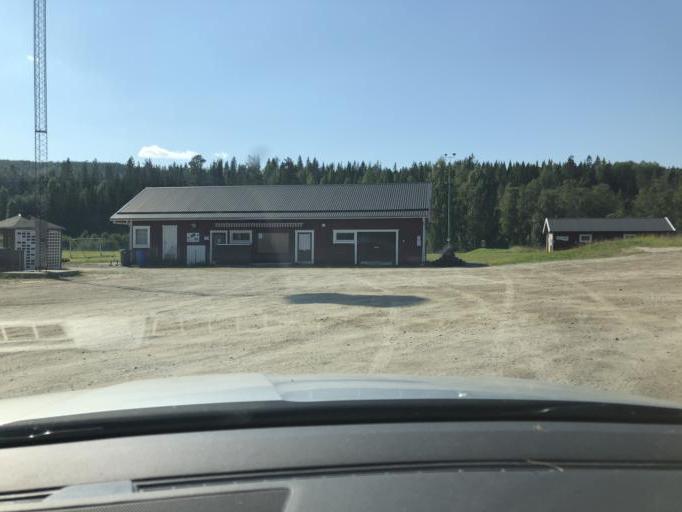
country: SE
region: Vaesternorrland
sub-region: OErnskoeldsviks Kommun
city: Bredbyn
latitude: 63.4453
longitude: 18.1051
